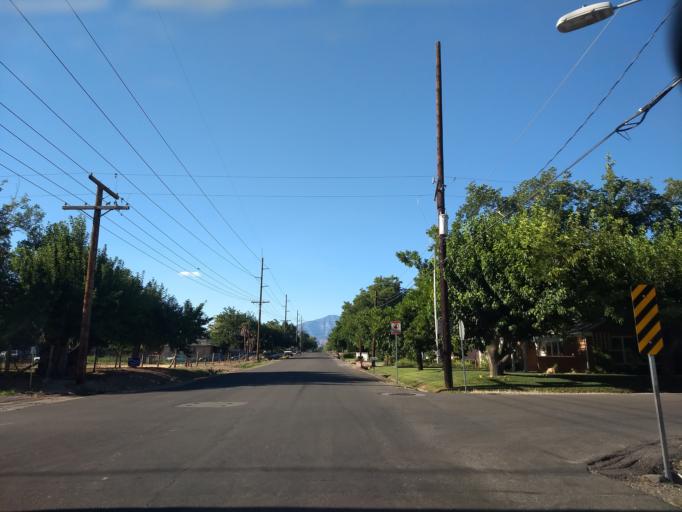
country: US
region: Utah
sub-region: Washington County
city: Washington
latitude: 37.1250
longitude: -113.5082
